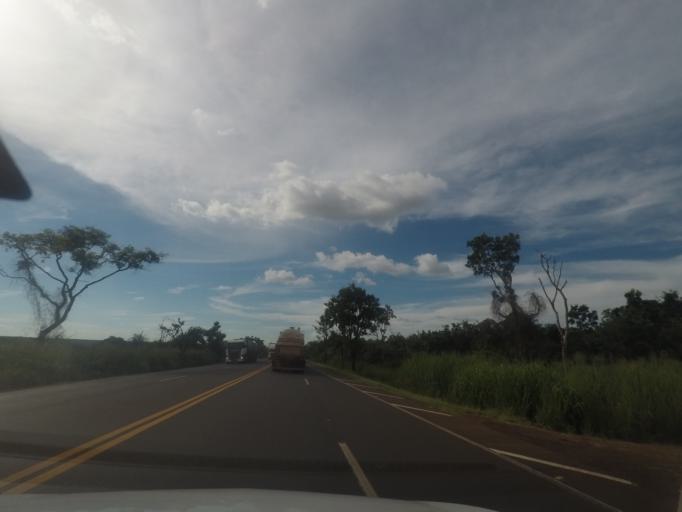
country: BR
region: Minas Gerais
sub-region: Monte Alegre De Minas
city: Monte Alegre de Minas
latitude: -19.0720
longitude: -49.0027
